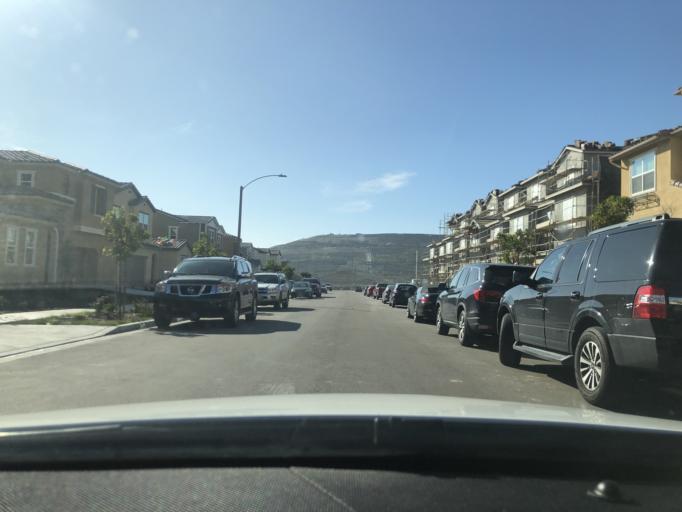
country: US
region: California
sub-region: San Diego County
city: Bonita
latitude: 32.6078
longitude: -116.9951
